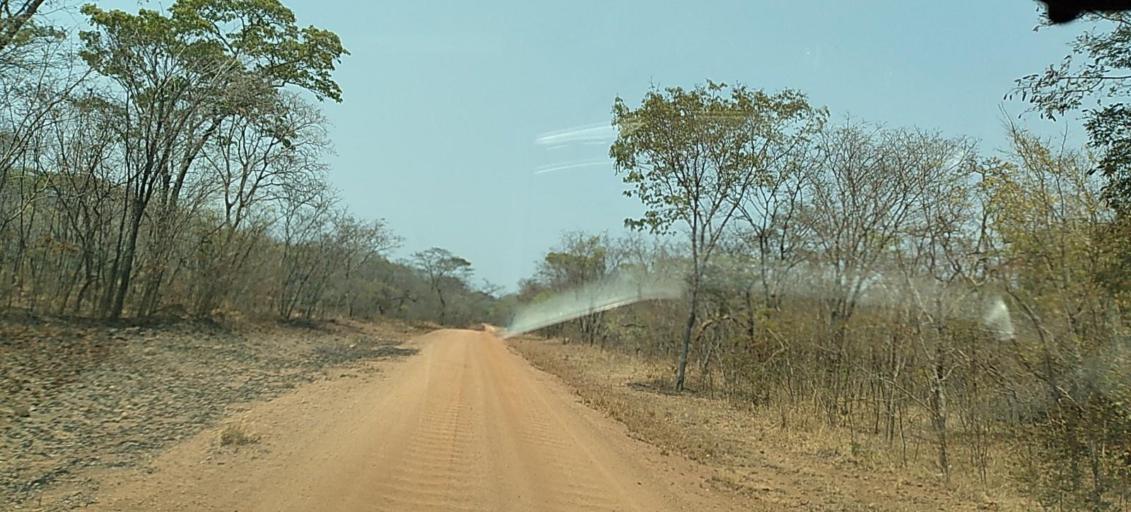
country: ZM
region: Central
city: Mumbwa
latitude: -14.2723
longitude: 26.5211
